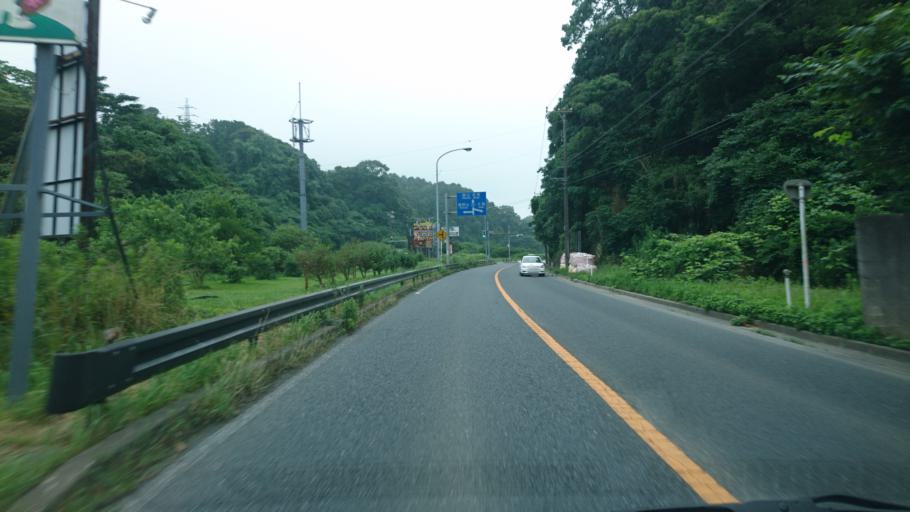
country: JP
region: Chiba
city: Kimitsu
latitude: 35.2774
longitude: 139.9101
